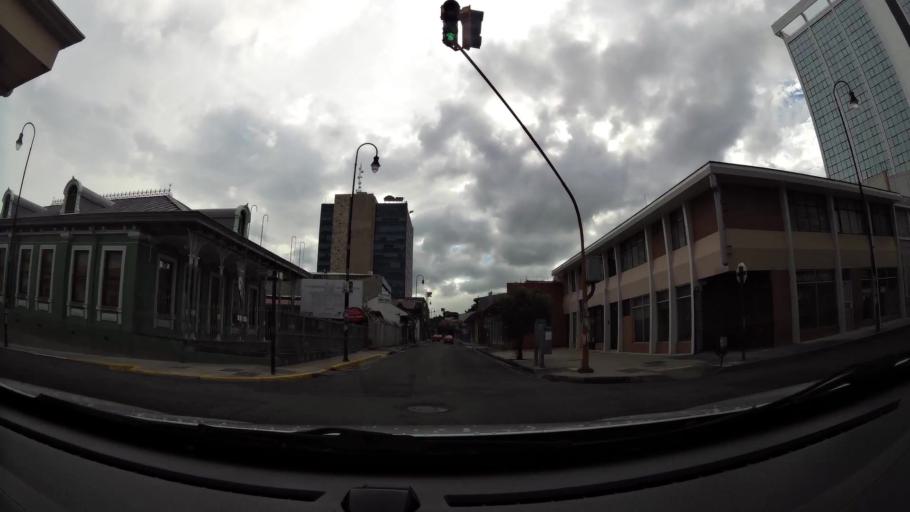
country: CR
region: San Jose
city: San Jose
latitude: 9.9369
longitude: -84.0758
